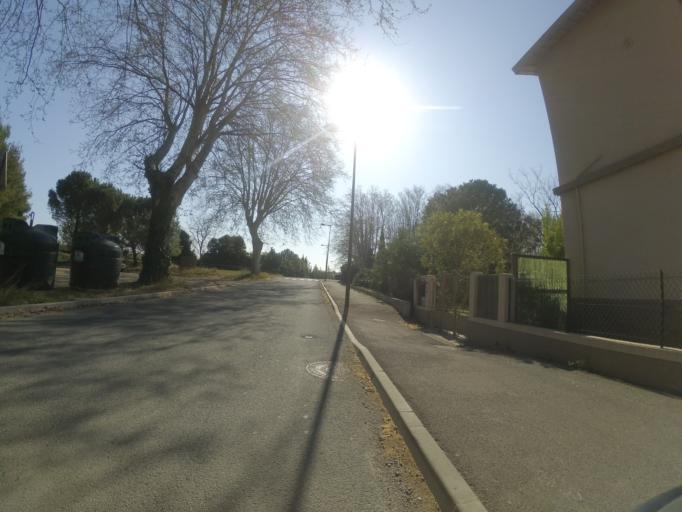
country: FR
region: Languedoc-Roussillon
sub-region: Departement des Pyrenees-Orientales
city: Thuir
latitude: 42.6365
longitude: 2.7509
